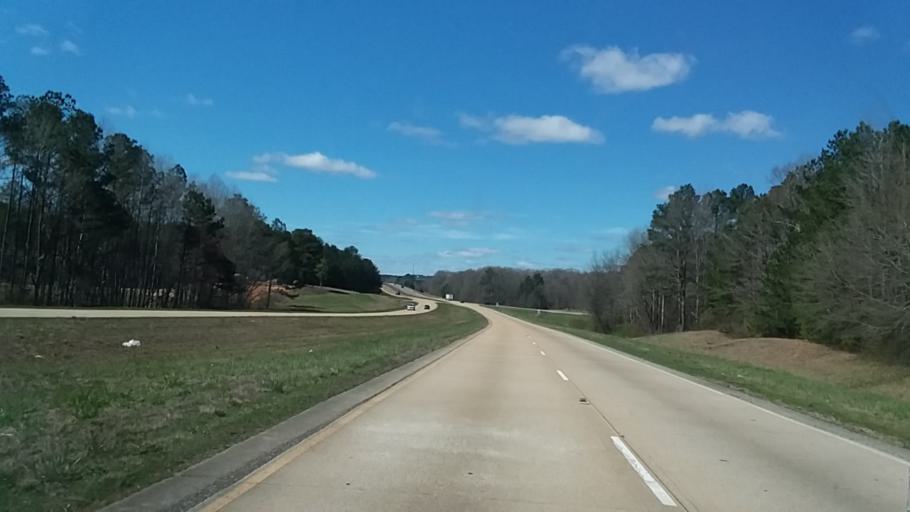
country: US
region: Mississippi
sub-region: Tishomingo County
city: Iuka
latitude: 34.8211
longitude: -88.2927
